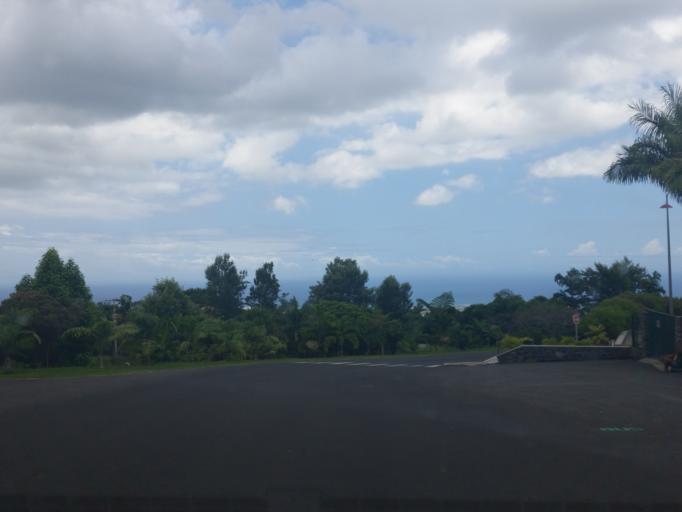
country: RE
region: Reunion
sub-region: Reunion
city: L'Entre-Deux
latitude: -21.2550
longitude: 55.4953
